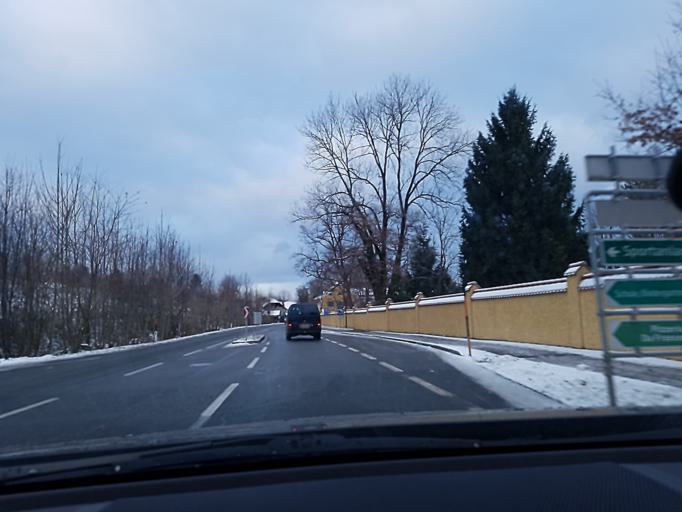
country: AT
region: Salzburg
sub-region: Politischer Bezirk Salzburg-Umgebung
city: Anif
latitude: 47.7441
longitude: 13.0681
